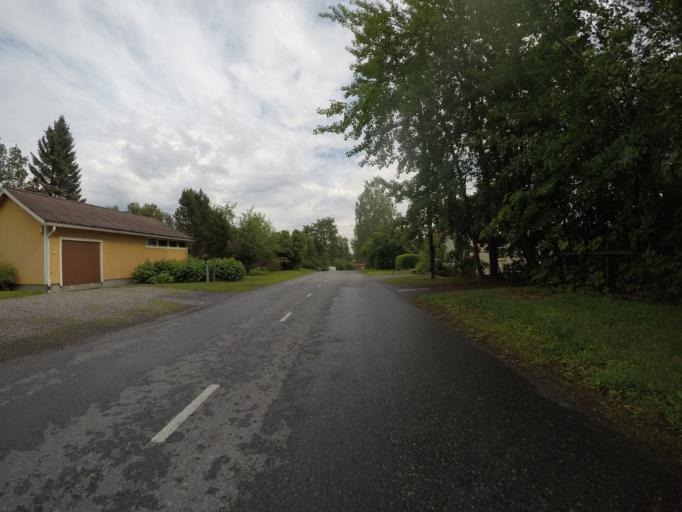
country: FI
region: Haeme
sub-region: Haemeenlinna
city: Haemeenlinna
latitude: 61.0052
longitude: 24.4888
